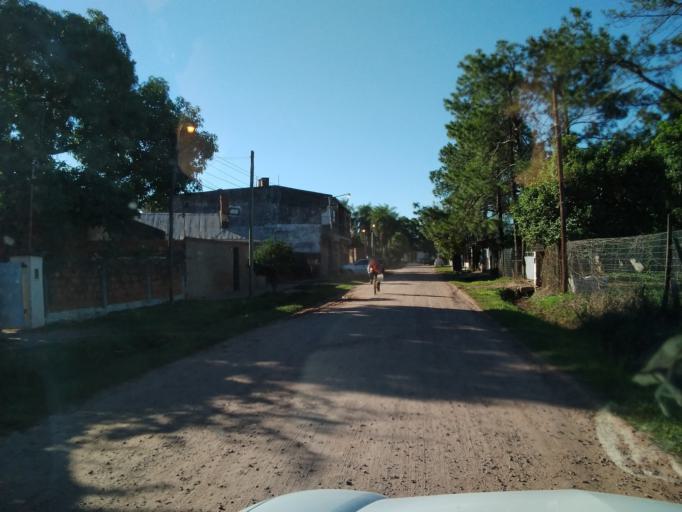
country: AR
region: Corrientes
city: Corrientes
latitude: -27.4700
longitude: -58.7960
